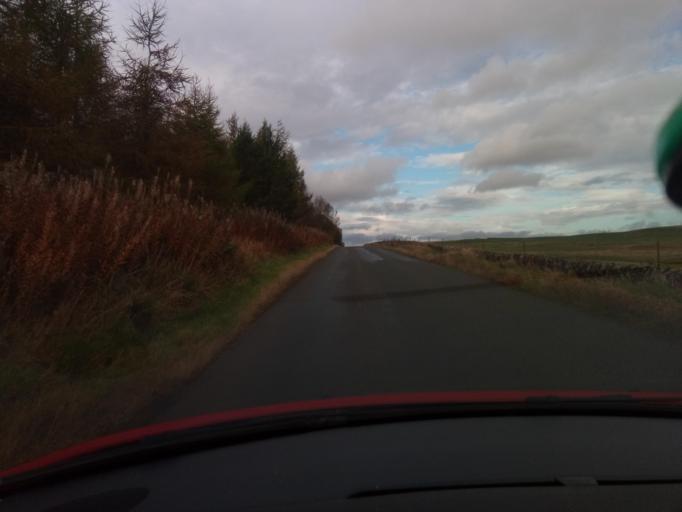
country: GB
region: Scotland
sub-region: South Lanarkshire
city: Carnwath
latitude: 55.7152
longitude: -3.5983
